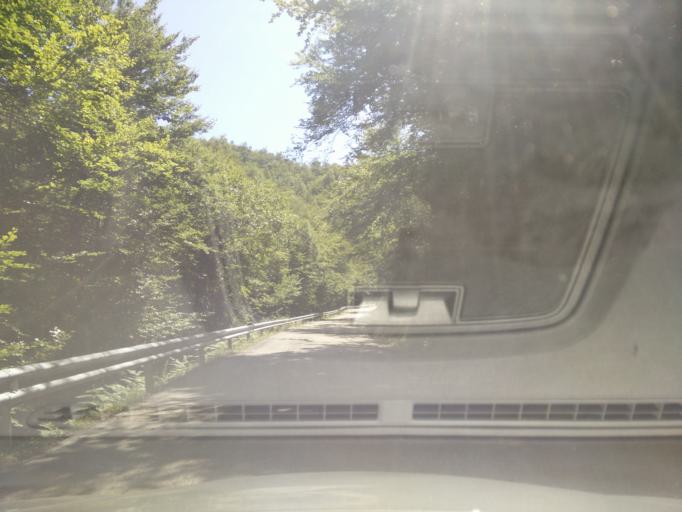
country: ES
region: Asturias
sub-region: Province of Asturias
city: Amieva
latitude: 43.1955
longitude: -5.1466
